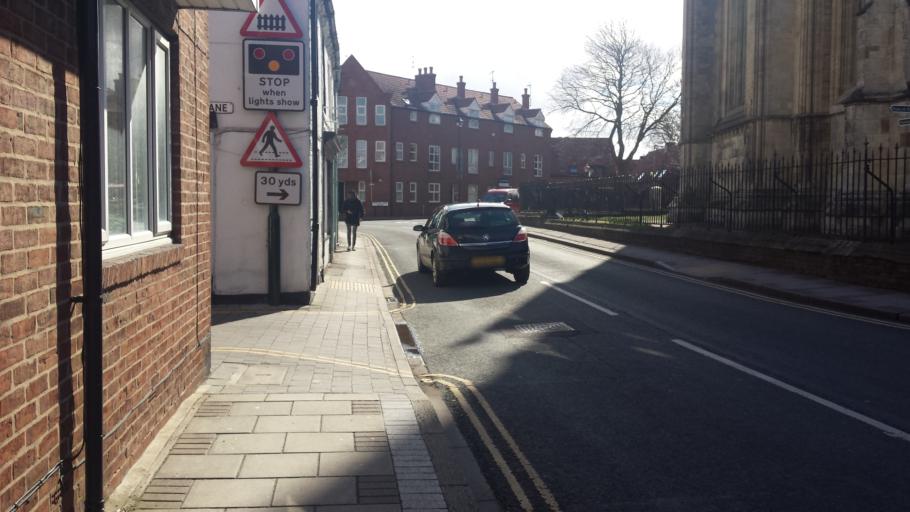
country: GB
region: England
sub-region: East Riding of Yorkshire
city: Beverley
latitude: 53.8397
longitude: -0.4240
